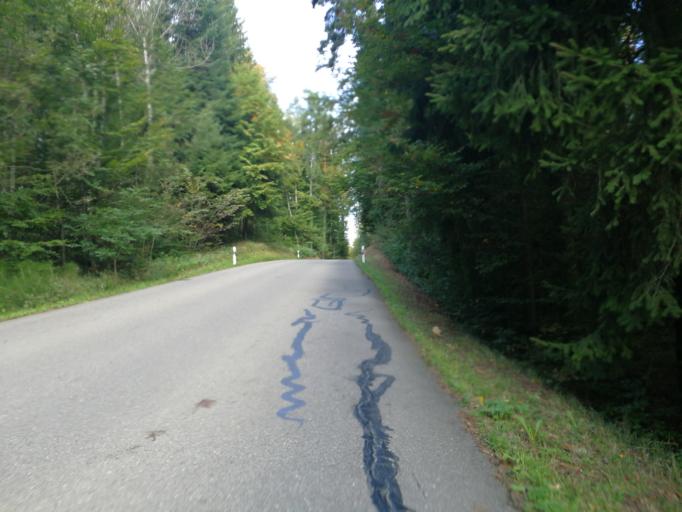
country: CH
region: Zurich
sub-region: Bezirk Meilen
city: Oetwil am See
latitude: 47.2673
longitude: 8.7101
